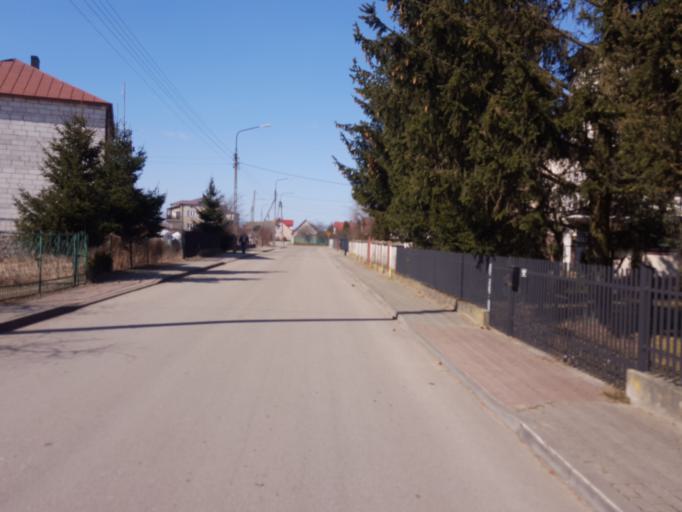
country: PL
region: Podlasie
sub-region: Powiat kolnenski
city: Stawiski
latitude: 53.3767
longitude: 22.1519
